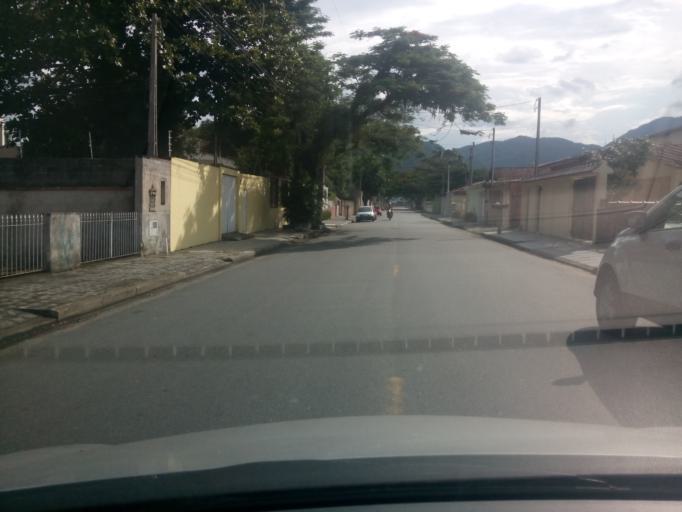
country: BR
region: Sao Paulo
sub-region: Peruibe
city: Peruibe
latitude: -24.3194
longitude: -47.0001
